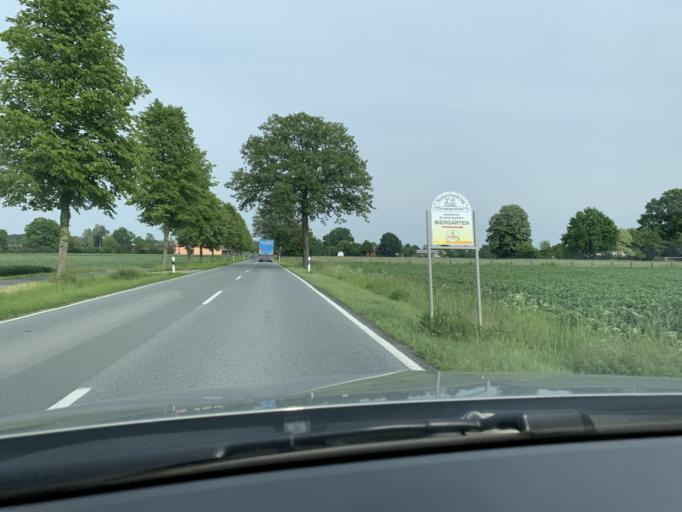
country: DE
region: North Rhine-Westphalia
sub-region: Regierungsbezirk Detmold
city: Langenberg
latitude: 51.7726
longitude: 8.3683
